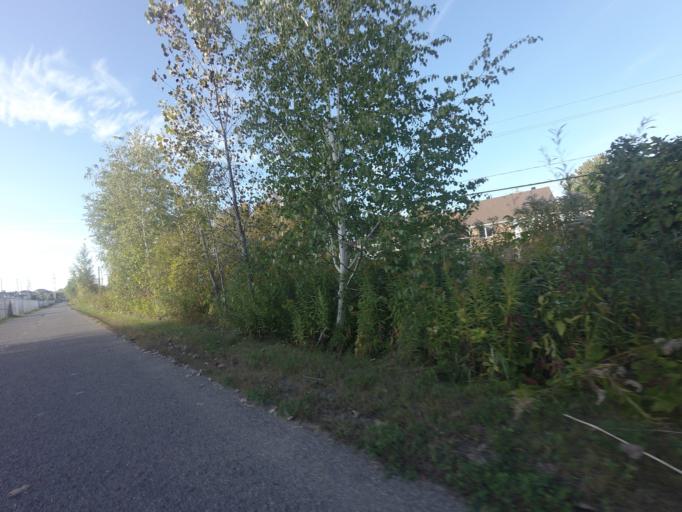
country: CA
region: Quebec
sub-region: Laurentides
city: Saint-Jerome
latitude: 45.7673
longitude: -73.9927
